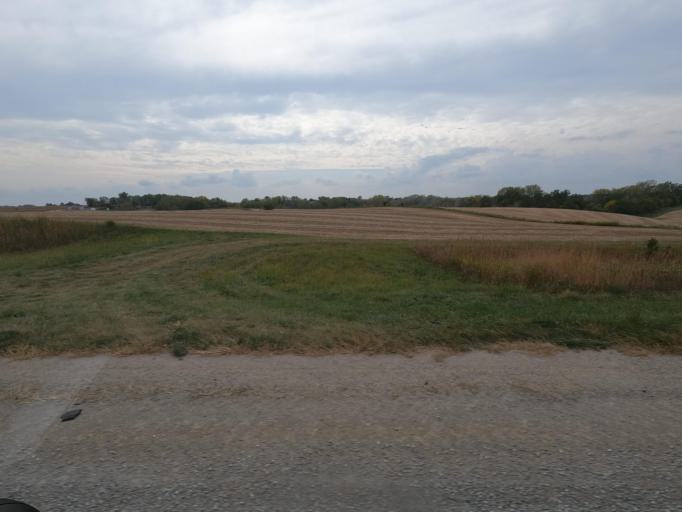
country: US
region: Iowa
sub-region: Jasper County
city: Monroe
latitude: 41.4571
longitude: -93.0333
